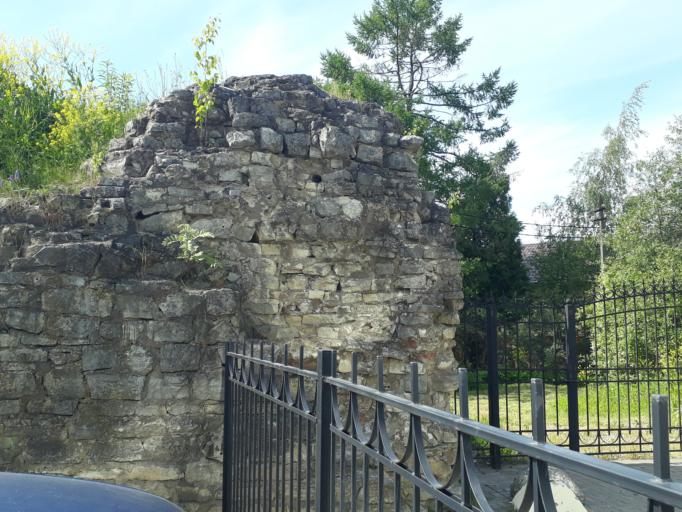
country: RU
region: St.-Petersburg
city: Pushkin
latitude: 59.7313
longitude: 30.4004
